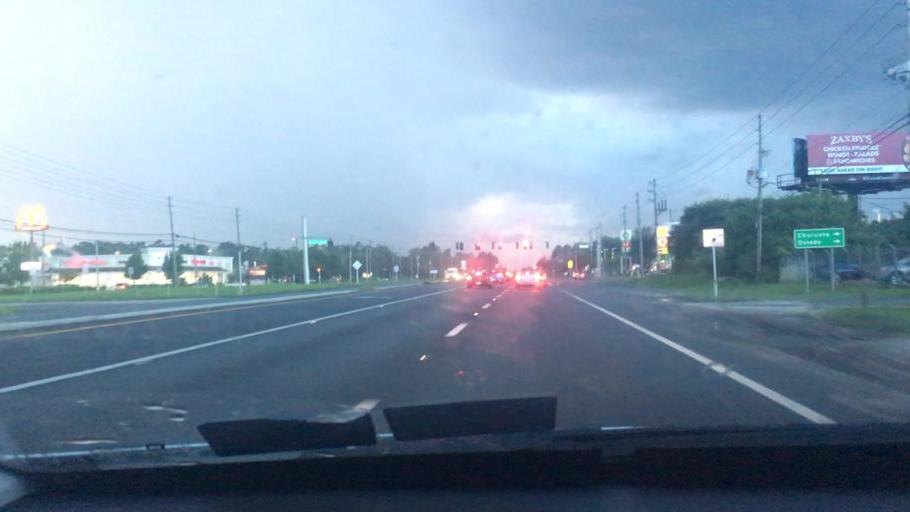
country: US
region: Florida
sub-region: Orange County
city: Bithlo
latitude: 28.5603
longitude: -81.1281
